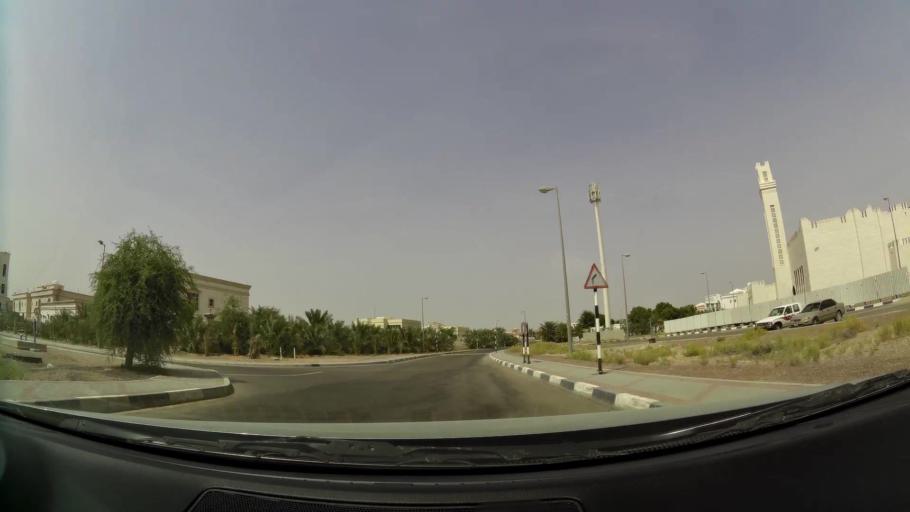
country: AE
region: Abu Dhabi
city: Al Ain
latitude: 24.1630
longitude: 55.6594
